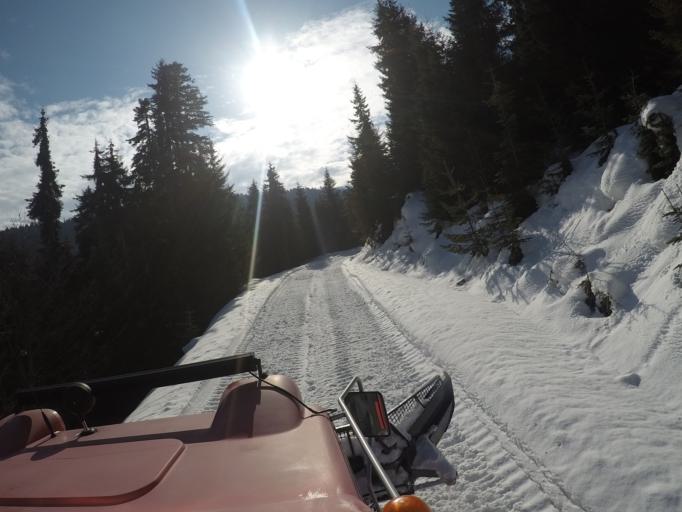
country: GE
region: Samtskhe-Javakheti
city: Adigeni
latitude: 41.6519
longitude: 42.6019
